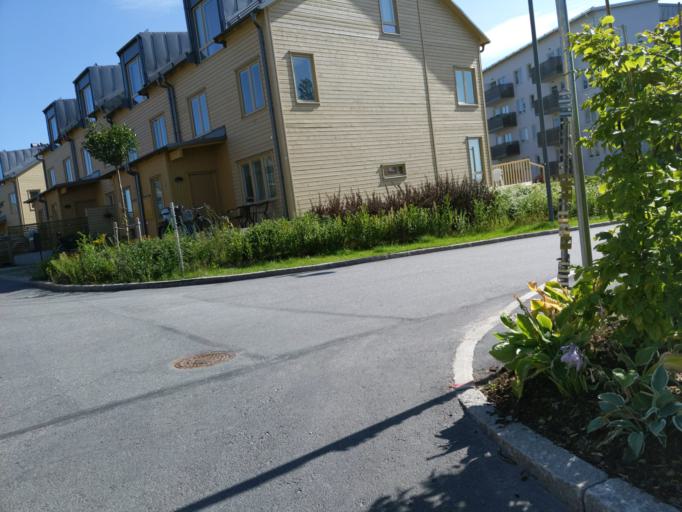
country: SE
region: Stockholm
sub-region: Solna Kommun
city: Rasunda
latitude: 59.3831
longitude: 17.9738
